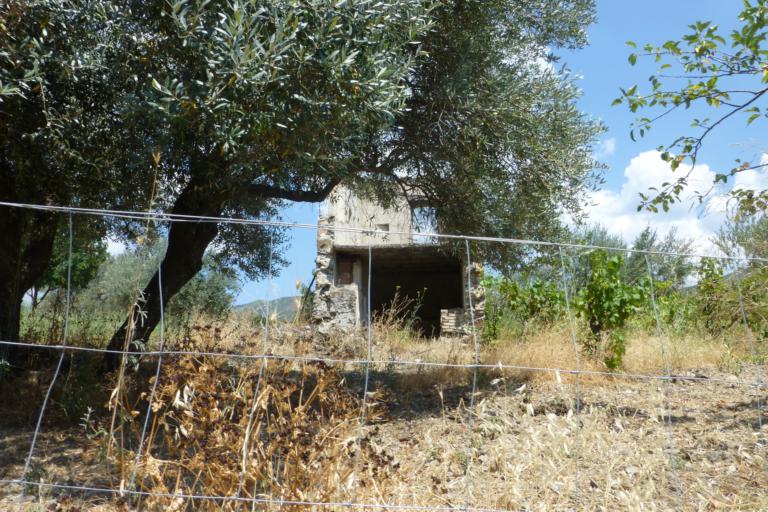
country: IT
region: Calabria
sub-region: Provincia di Reggio Calabria
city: Pazzano
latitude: 38.4799
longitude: 16.4409
